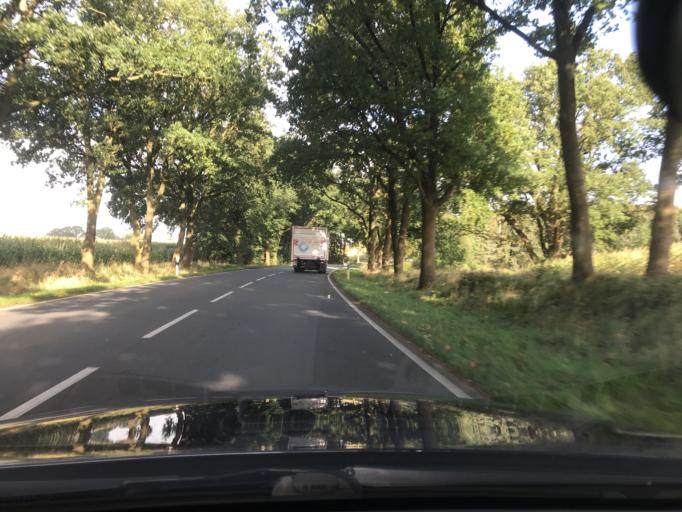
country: DE
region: Lower Saxony
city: Harsefeld
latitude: 53.4699
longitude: 9.4940
